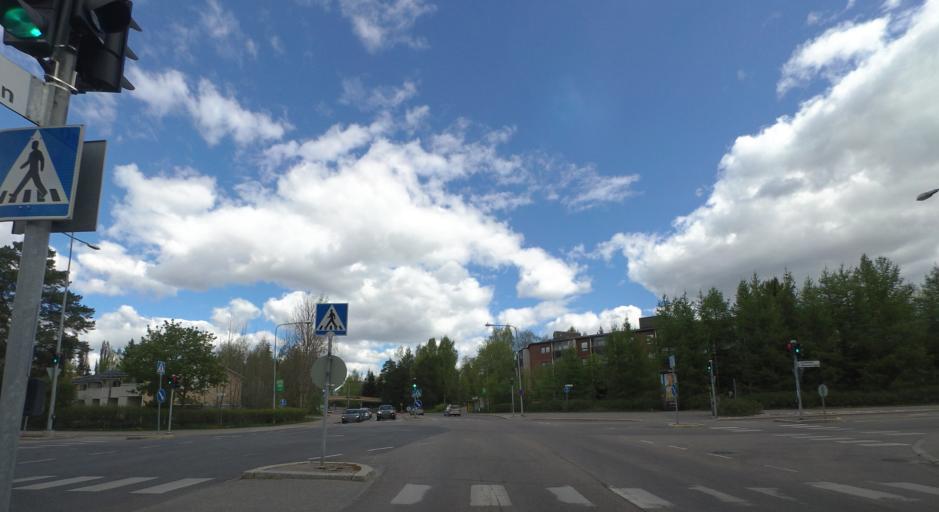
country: FI
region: Uusimaa
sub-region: Helsinki
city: Vantaa
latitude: 60.2969
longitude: 25.0346
